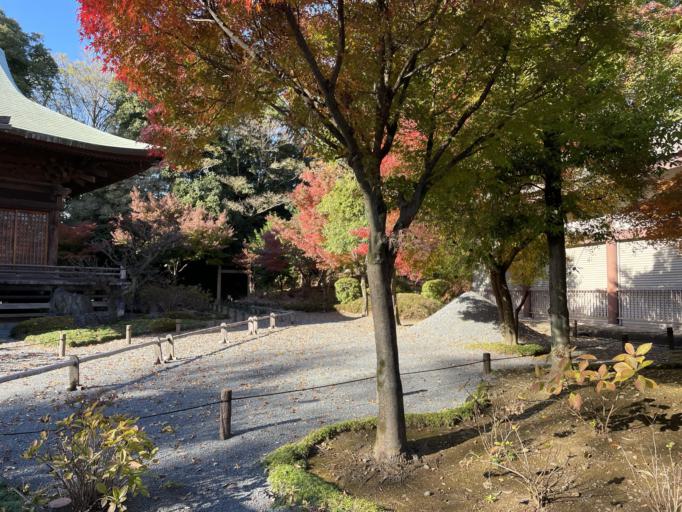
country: JP
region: Saitama
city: Wako
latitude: 35.7917
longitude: 139.6346
